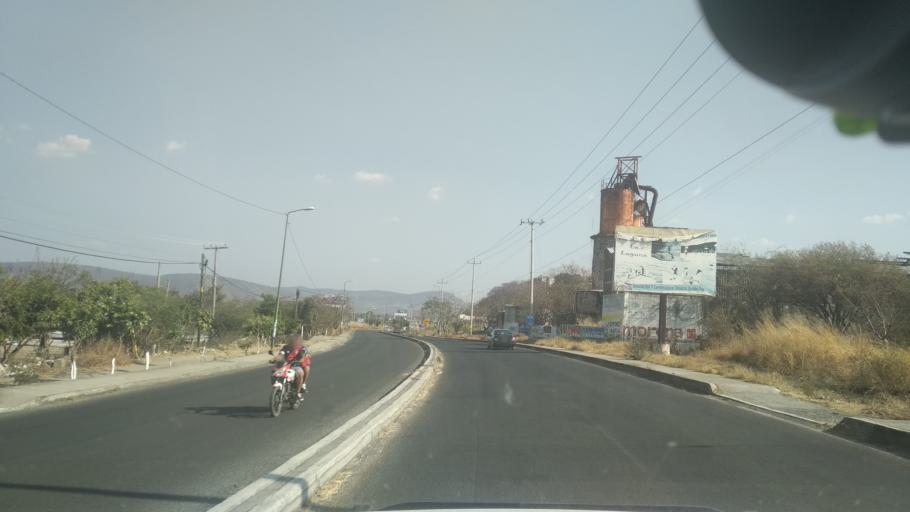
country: MX
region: Puebla
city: Izucar de Matamoros
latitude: 18.6193
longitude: -98.4706
